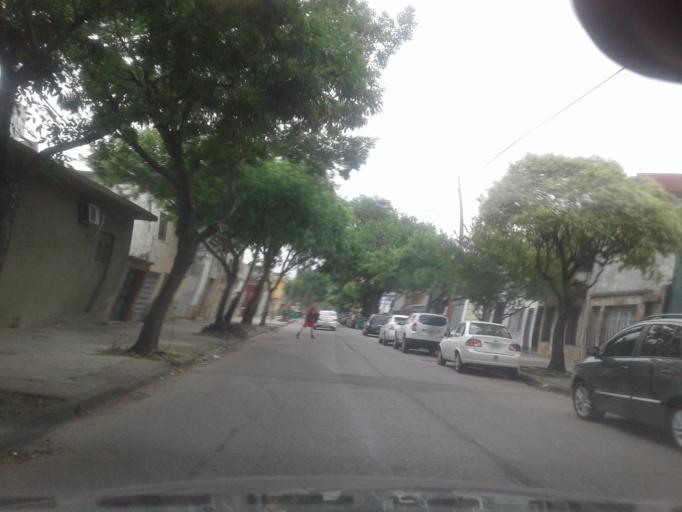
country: AR
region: Santa Fe
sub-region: Departamento de Rosario
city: Rosario
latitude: -32.9651
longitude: -60.6646
